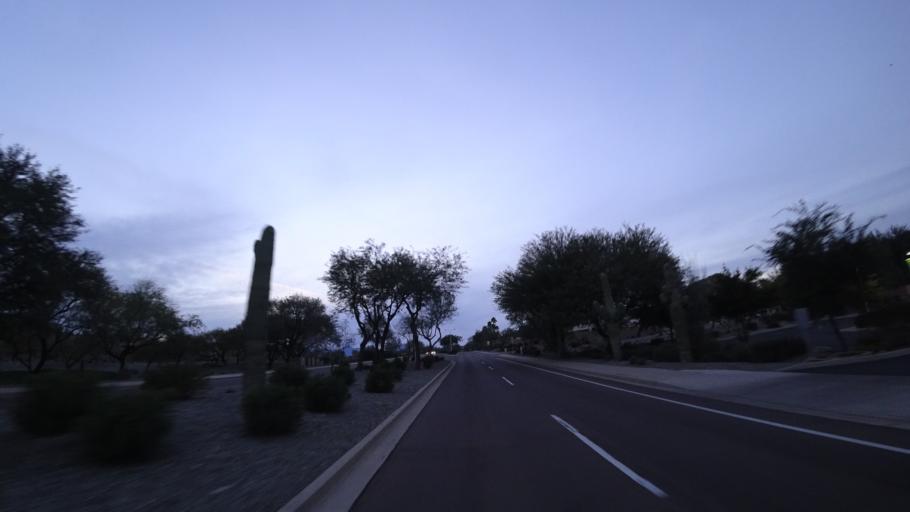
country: US
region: Arizona
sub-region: Maricopa County
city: Guadalupe
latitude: 33.3051
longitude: -112.0399
